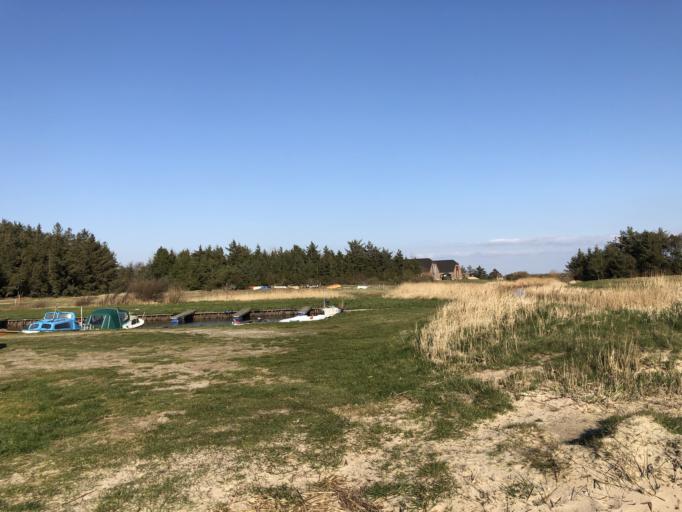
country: DK
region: Central Jutland
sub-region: Holstebro Kommune
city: Ulfborg
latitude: 56.3505
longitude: 8.2440
